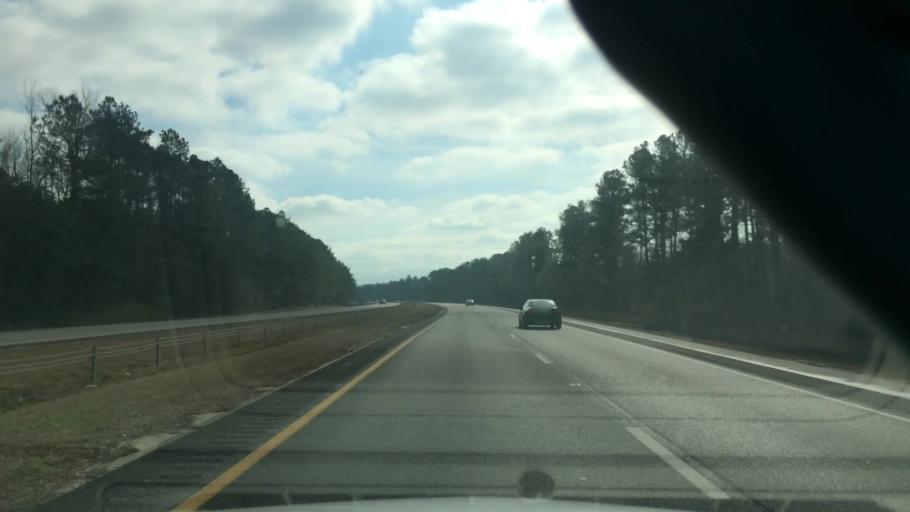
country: US
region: North Carolina
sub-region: Pender County
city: Burgaw
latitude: 34.5388
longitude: -77.8935
